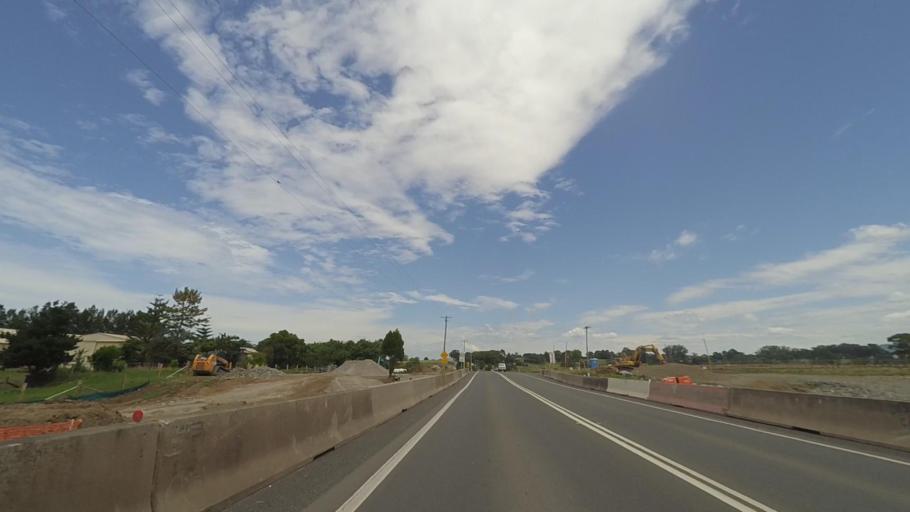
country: AU
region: New South Wales
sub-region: Shoalhaven Shire
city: Berry
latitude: -34.7863
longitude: 150.6755
